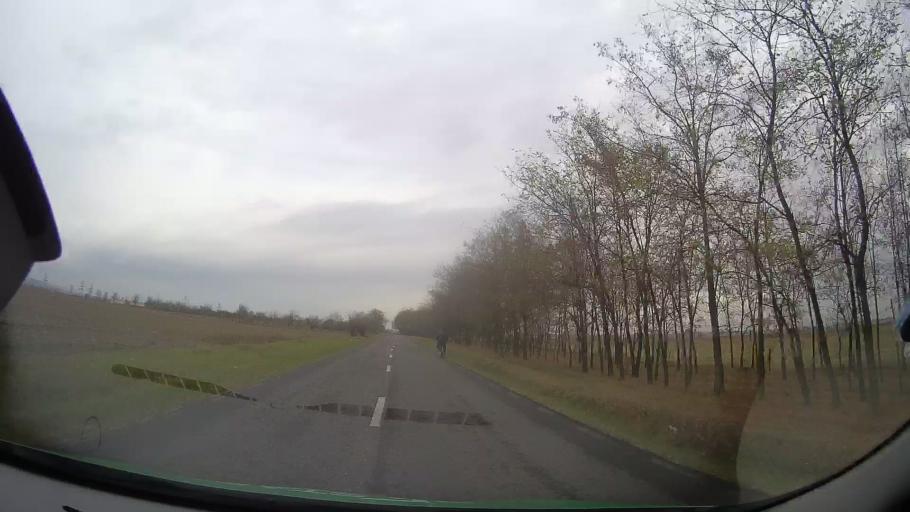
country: RO
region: Prahova
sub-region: Comuna Berceni
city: Berceni
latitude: 44.9393
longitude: 26.1100
